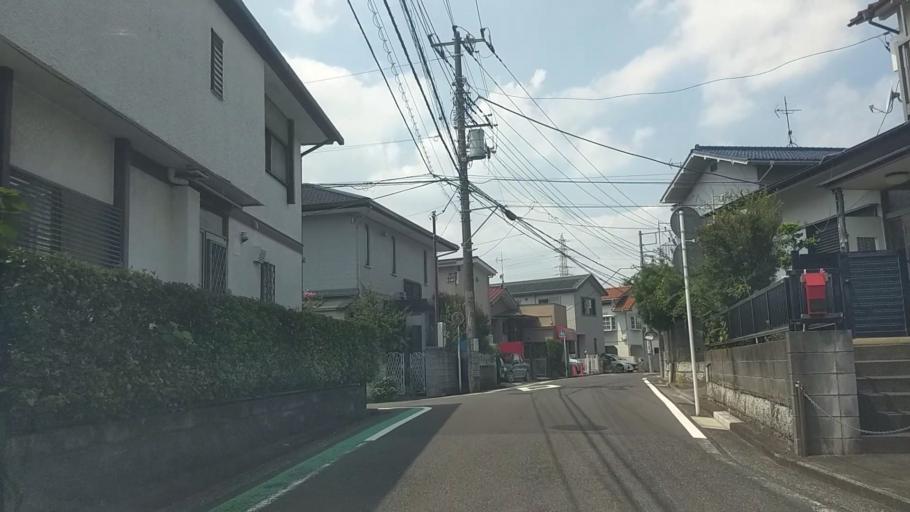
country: JP
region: Kanagawa
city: Yokohama
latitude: 35.4908
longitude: 139.6174
